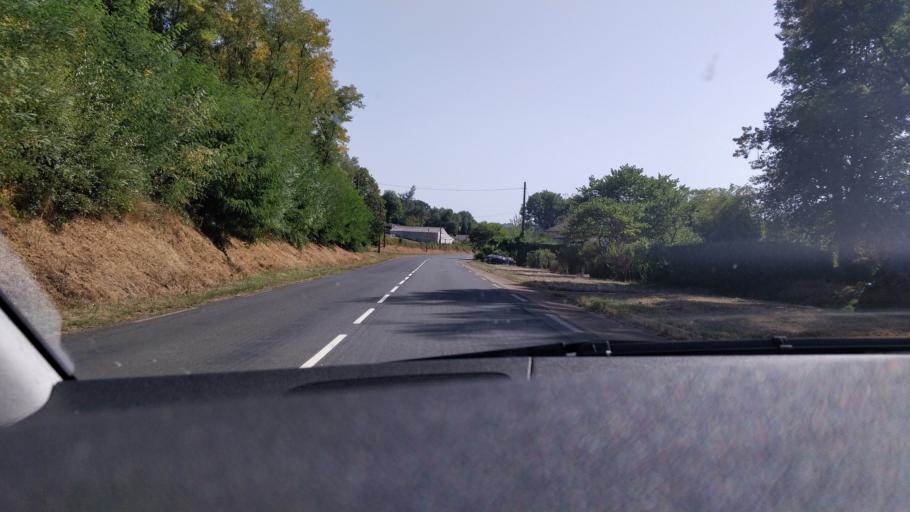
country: FR
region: Limousin
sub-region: Departement de la Correze
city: Uzerche
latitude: 45.4503
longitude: 1.5594
